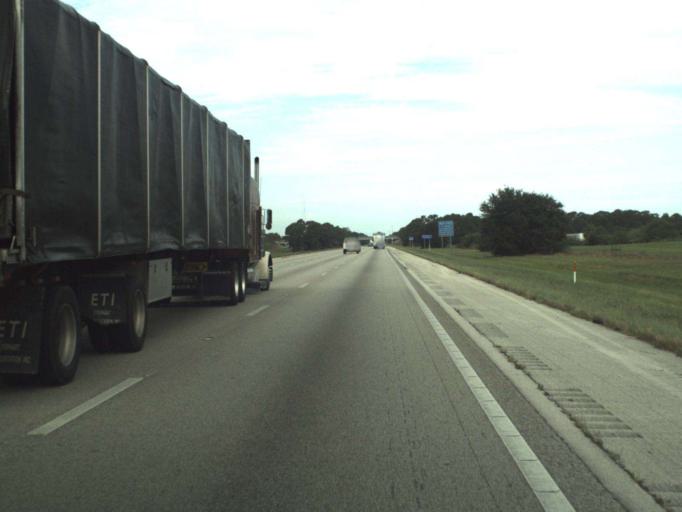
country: US
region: Florida
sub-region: Martin County
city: Palm City
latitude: 27.1274
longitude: -80.3096
